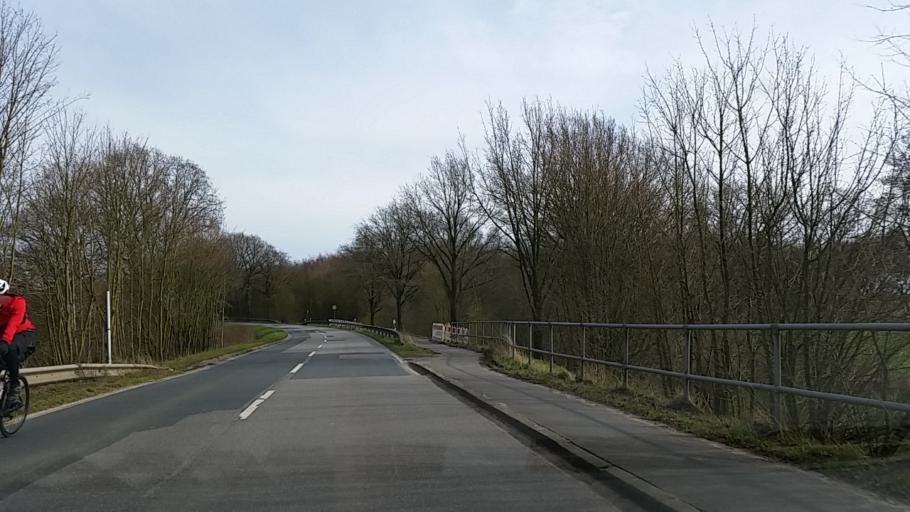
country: DE
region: Schleswig-Holstein
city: Stapelfeld
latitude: 53.5686
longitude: 10.2280
